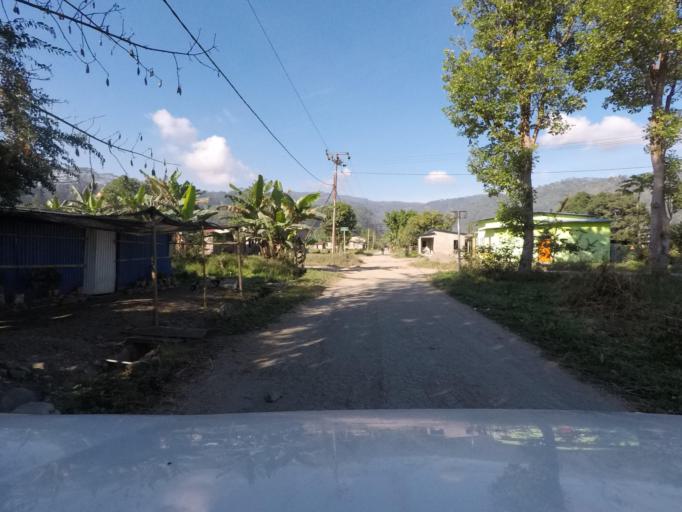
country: TL
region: Ermera
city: Gleno
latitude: -8.7258
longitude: 125.4341
